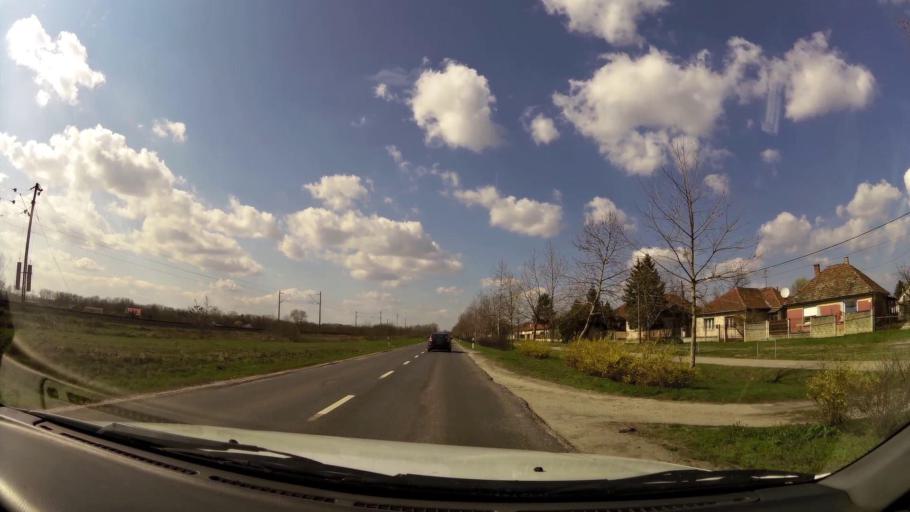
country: HU
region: Pest
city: Nagykata
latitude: 47.3998
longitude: 19.7559
